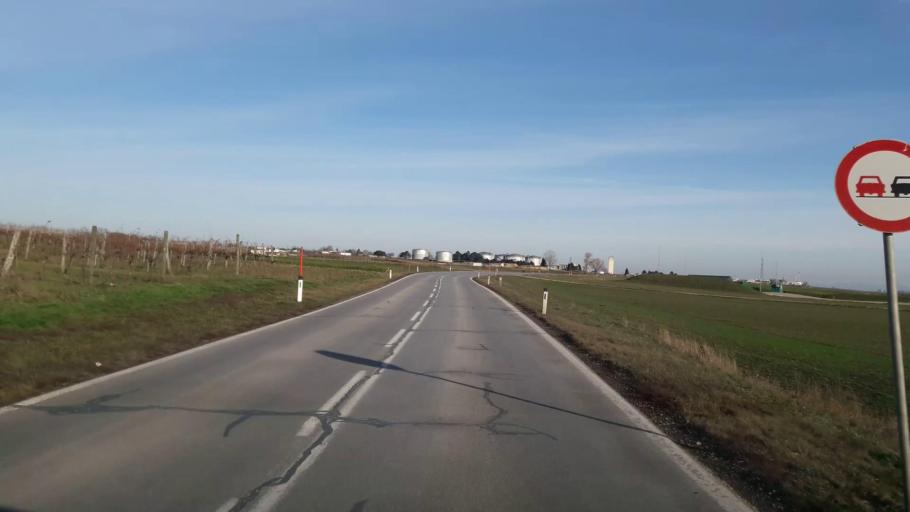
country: AT
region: Lower Austria
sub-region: Politischer Bezirk Mistelbach
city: Bockfliess
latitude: 48.3621
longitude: 16.6173
